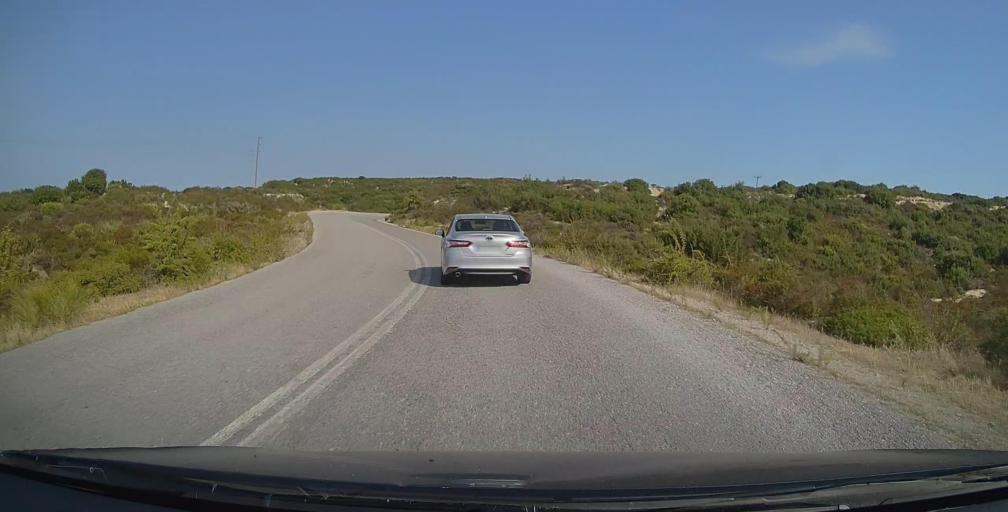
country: GR
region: Central Macedonia
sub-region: Nomos Chalkidikis
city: Sykia
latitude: 39.9786
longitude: 23.9594
